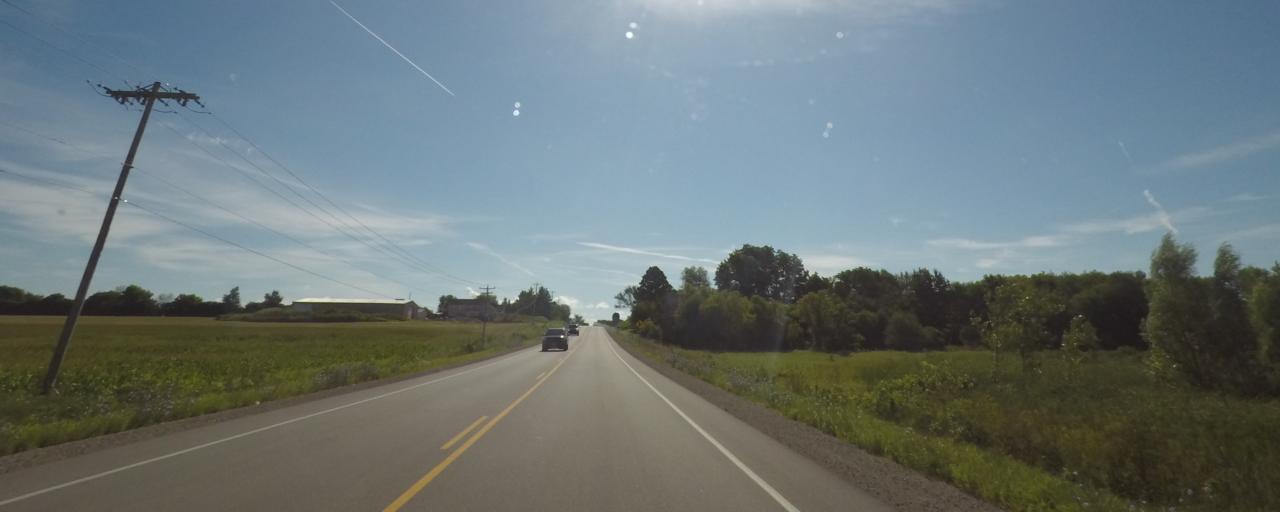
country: US
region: Wisconsin
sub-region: Jefferson County
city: Johnson Creek
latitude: 43.0757
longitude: -88.7314
